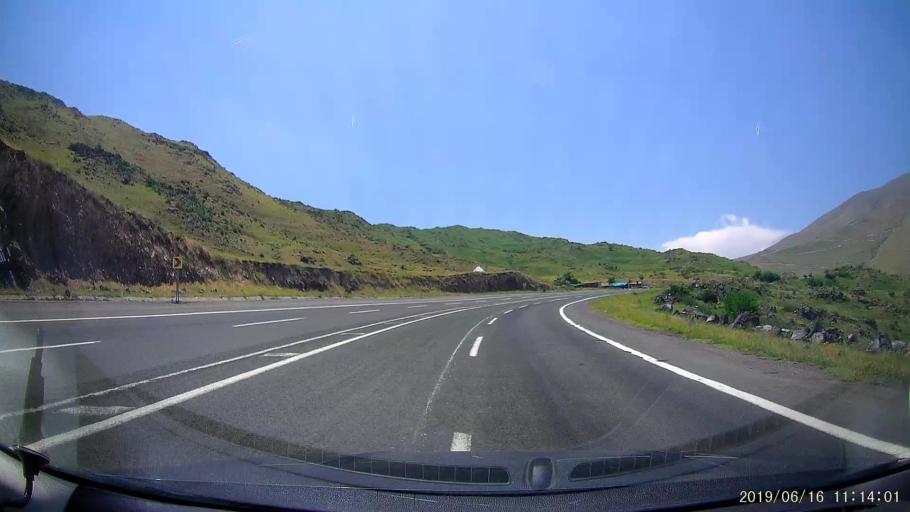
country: TR
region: Igdir
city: Igdir
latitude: 39.7847
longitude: 44.1463
